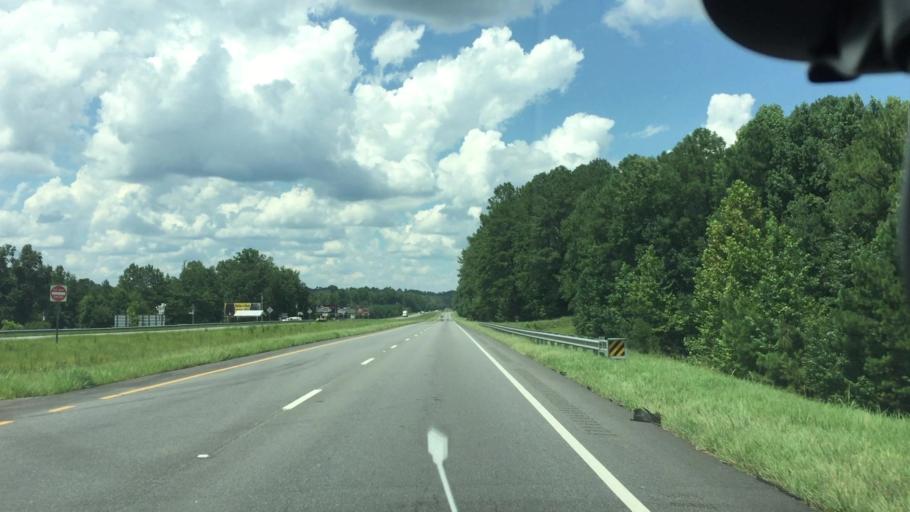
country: US
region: Alabama
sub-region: Pike County
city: Troy
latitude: 31.9176
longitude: -86.0146
